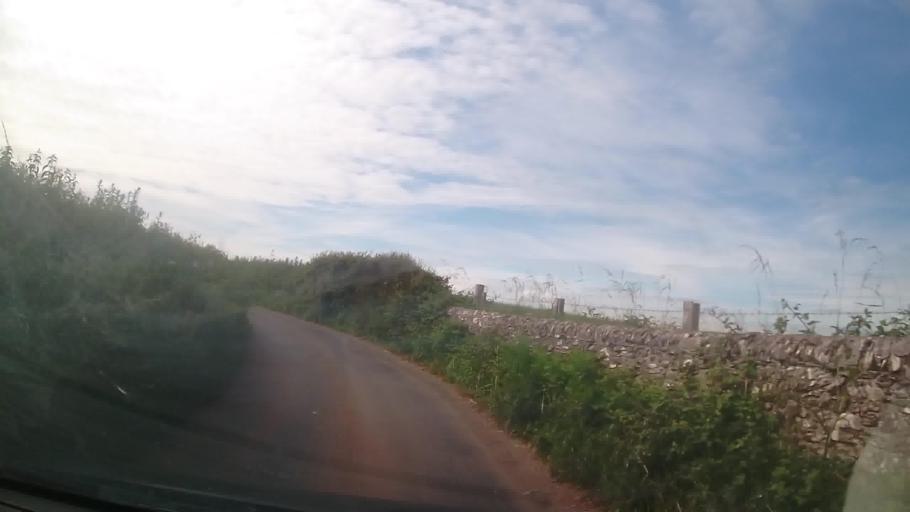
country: GB
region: England
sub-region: Devon
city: Salcombe
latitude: 50.2369
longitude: -3.6747
